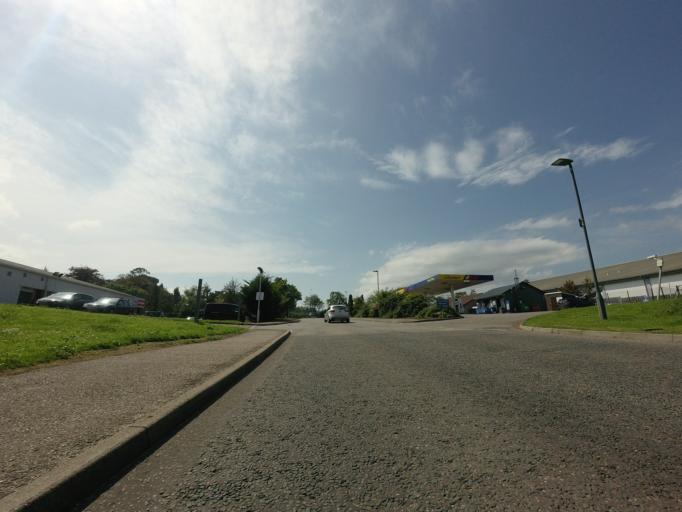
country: GB
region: Scotland
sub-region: Highland
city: Tain
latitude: 57.8171
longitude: -4.0657
